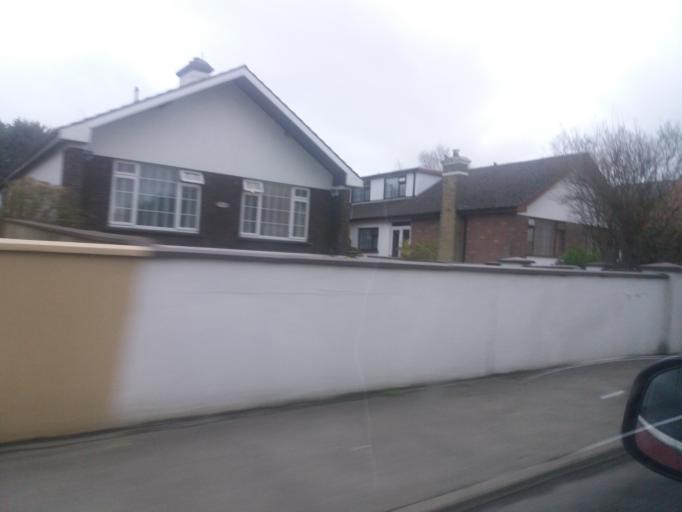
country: IE
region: Munster
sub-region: County Limerick
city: Abbeyfeale
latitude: 52.3801
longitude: -9.3031
